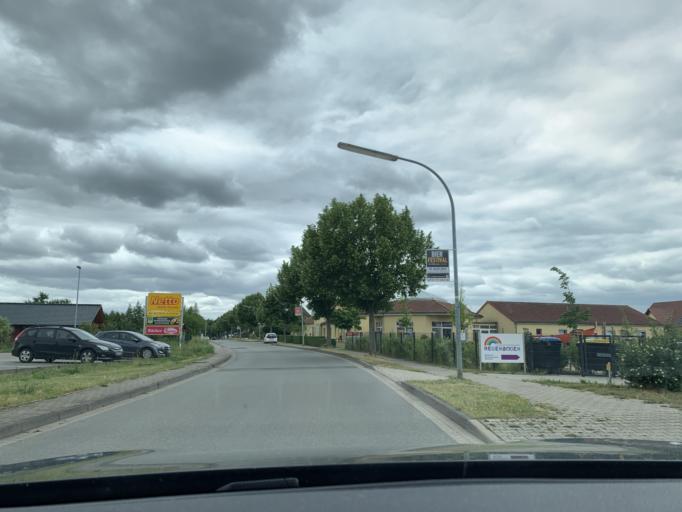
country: DE
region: Mecklenburg-Vorpommern
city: Rechlin
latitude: 53.3251
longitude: 12.7180
